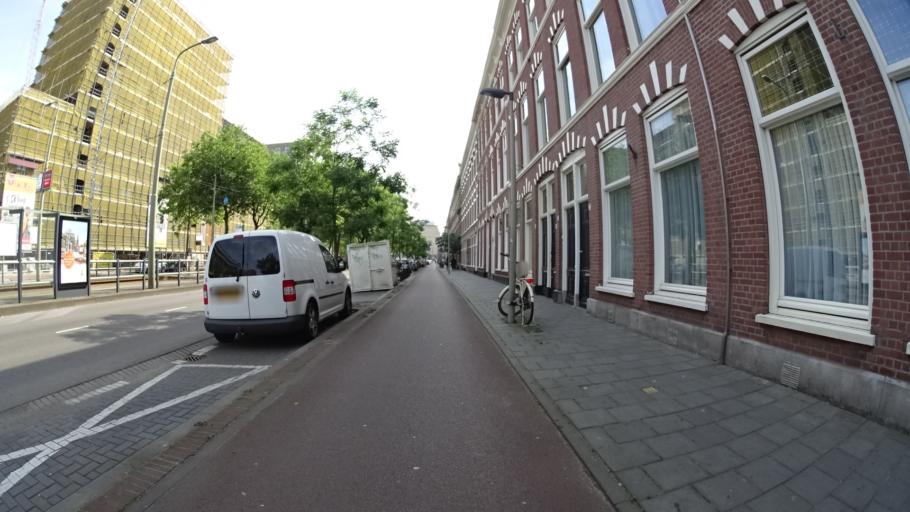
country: NL
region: South Holland
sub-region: Gemeente Den Haag
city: The Hague
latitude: 52.0729
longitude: 4.2931
